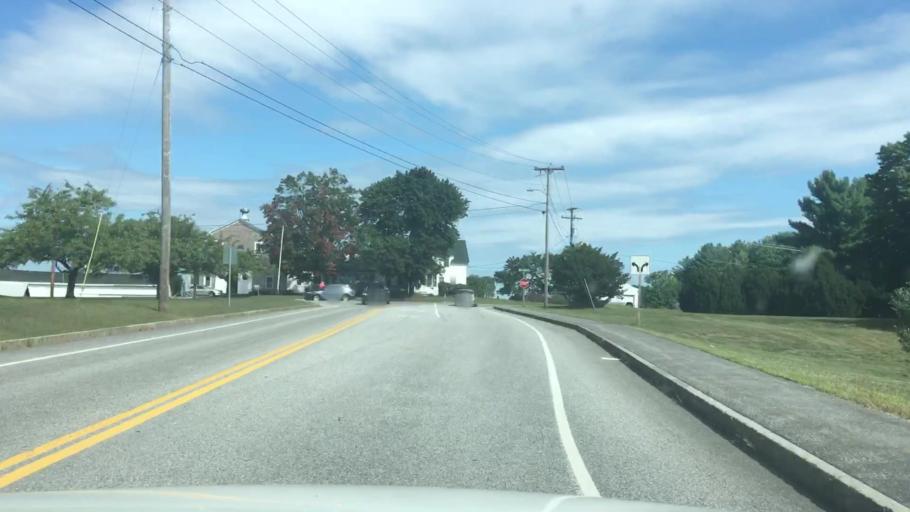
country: US
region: Maine
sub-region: Androscoggin County
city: Auburn
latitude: 44.1212
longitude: -70.2501
